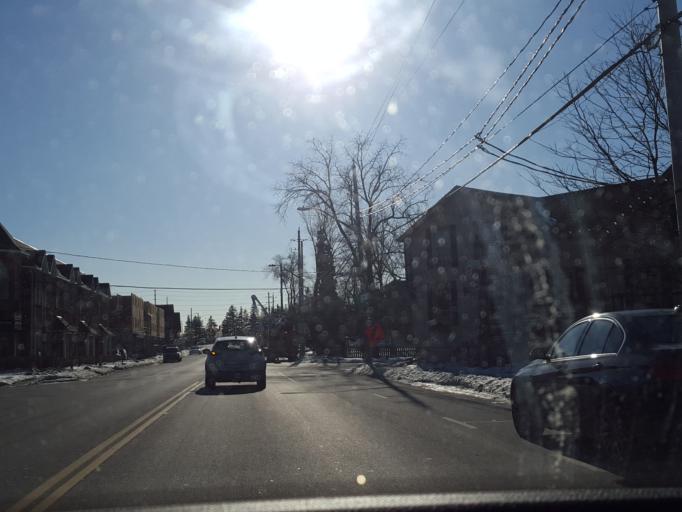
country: CA
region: Ontario
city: Oshawa
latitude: 43.9564
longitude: -78.9610
